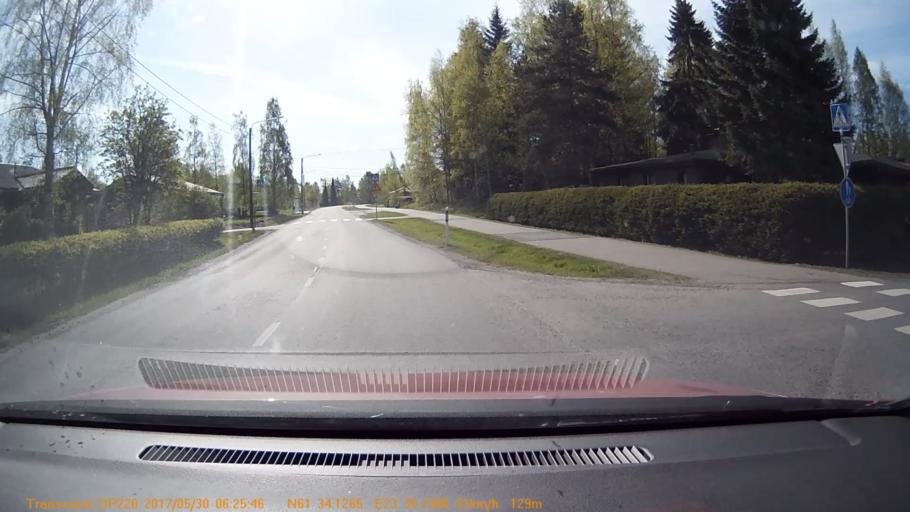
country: FI
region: Pirkanmaa
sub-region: Tampere
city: Yloejaervi
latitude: 61.5689
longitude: 23.5864
